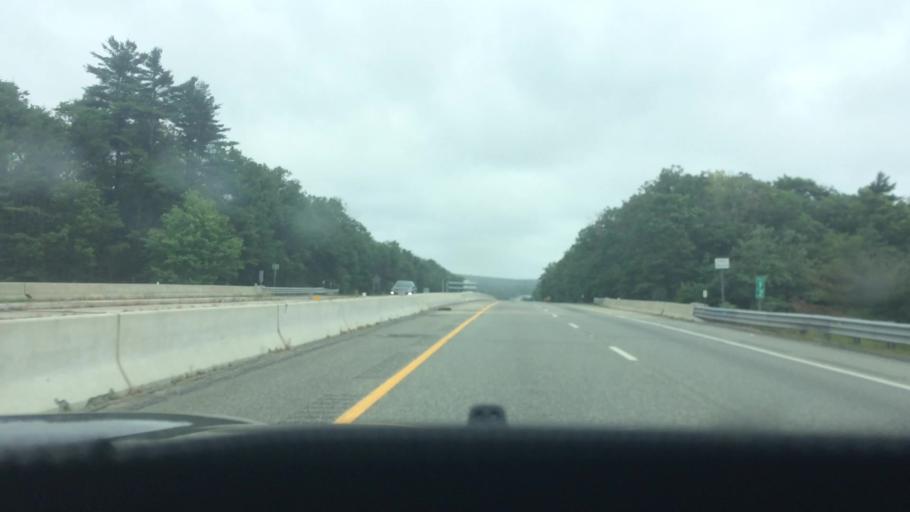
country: US
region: Rhode Island
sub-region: Washington County
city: Hope Valley
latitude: 41.5384
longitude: -71.6786
